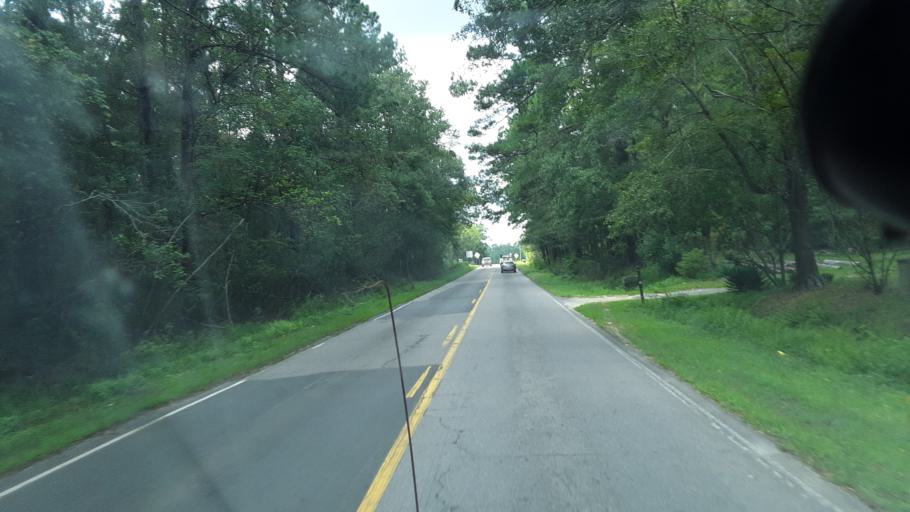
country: US
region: South Carolina
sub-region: Williamsburg County
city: Andrews
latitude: 33.3655
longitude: -79.4562
